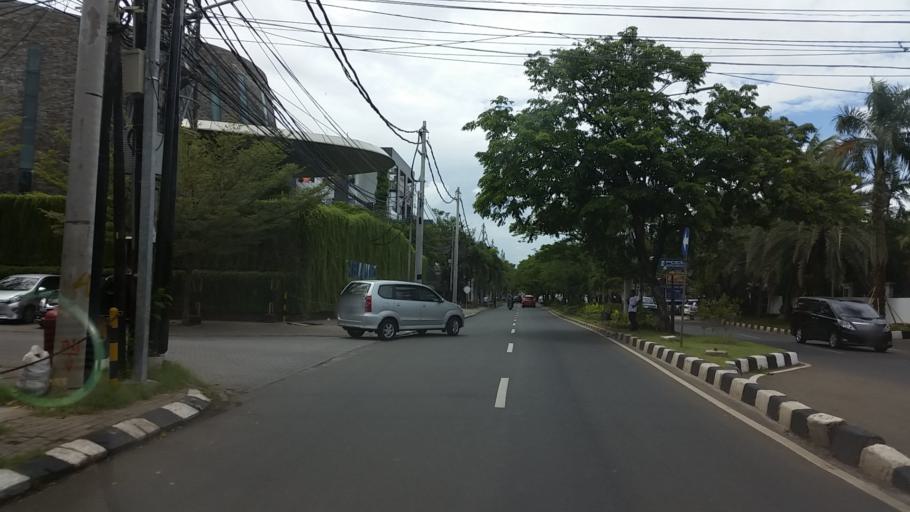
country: ID
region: Jakarta Raya
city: Jakarta
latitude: -6.1123
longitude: 106.7922
